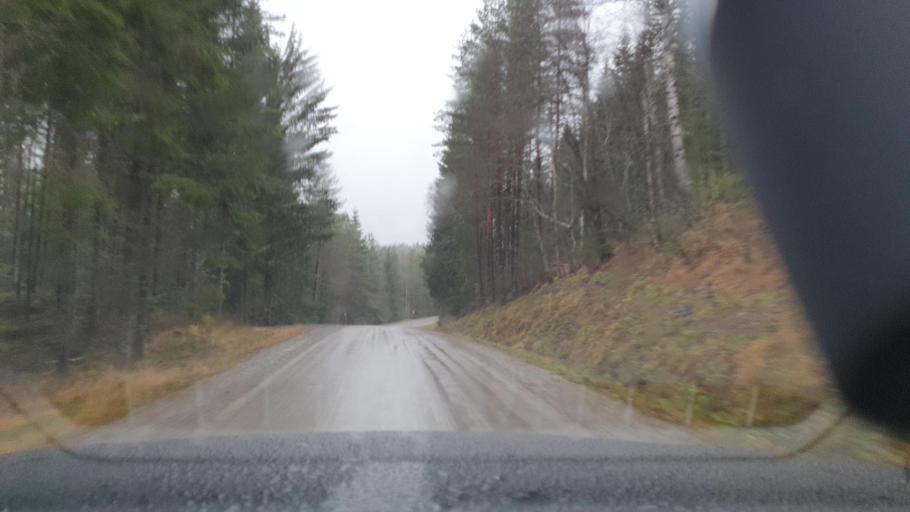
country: SE
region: Vaermland
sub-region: Arvika Kommun
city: Arvika
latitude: 59.8563
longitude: 12.7158
